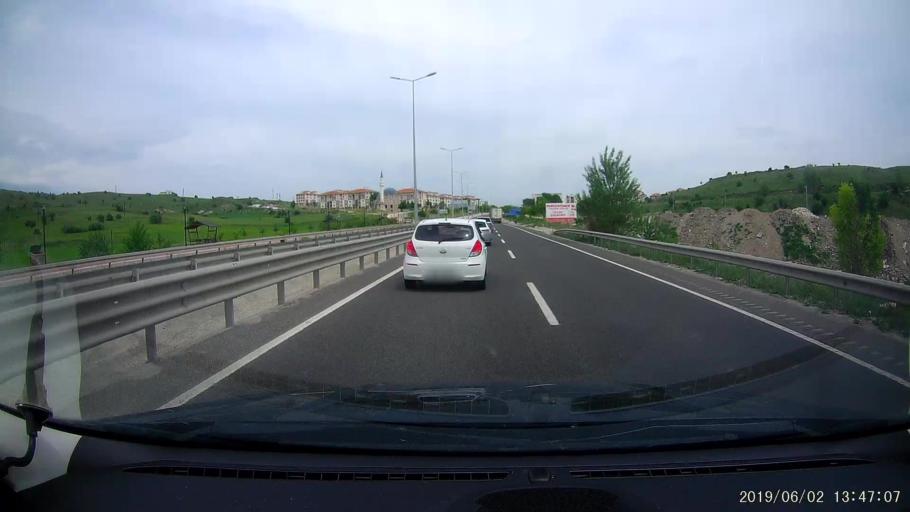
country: TR
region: Cankiri
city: Kursunlu
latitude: 40.8400
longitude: 33.2772
